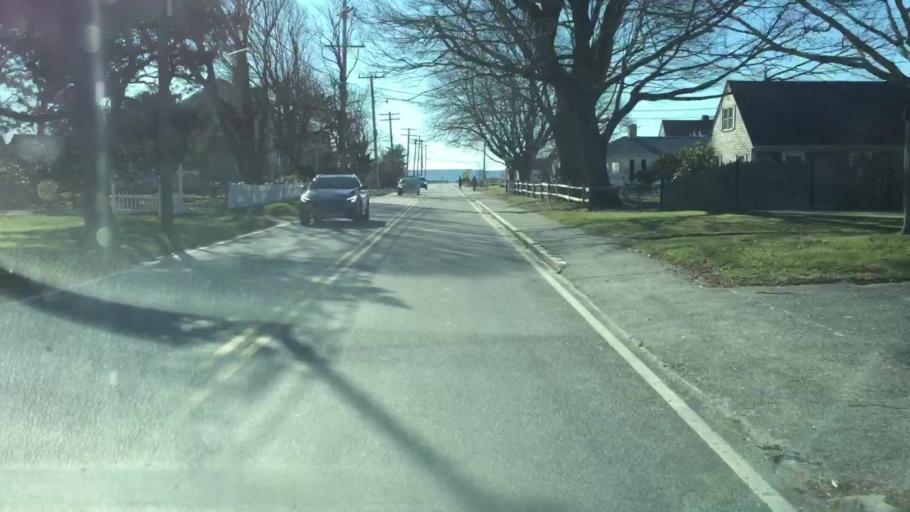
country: US
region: Massachusetts
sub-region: Barnstable County
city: Falmouth
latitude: 41.5448
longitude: -70.6154
